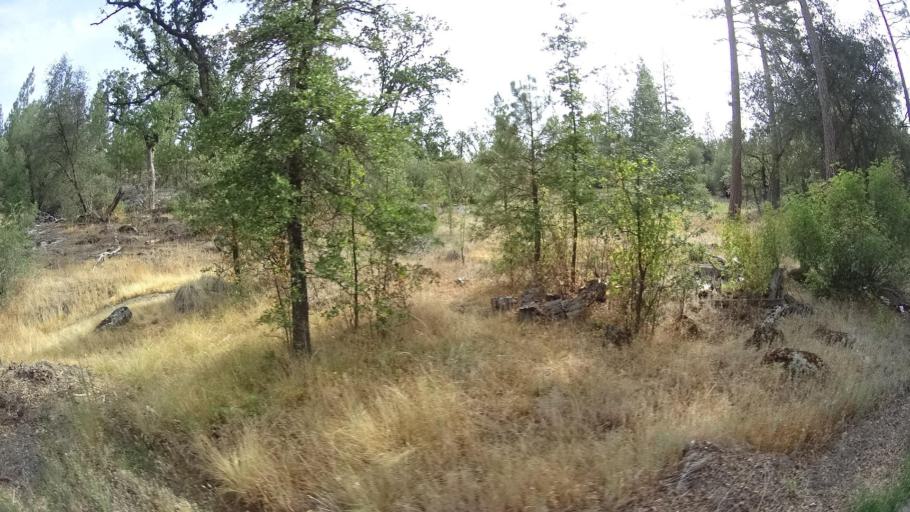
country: US
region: California
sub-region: Madera County
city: Ahwahnee
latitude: 37.4654
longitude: -119.7953
